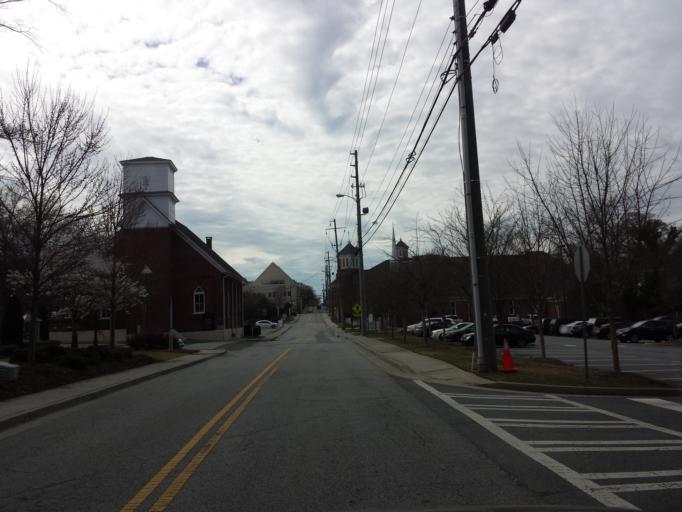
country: US
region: Georgia
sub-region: Cobb County
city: Marietta
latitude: 33.9553
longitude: -84.5466
